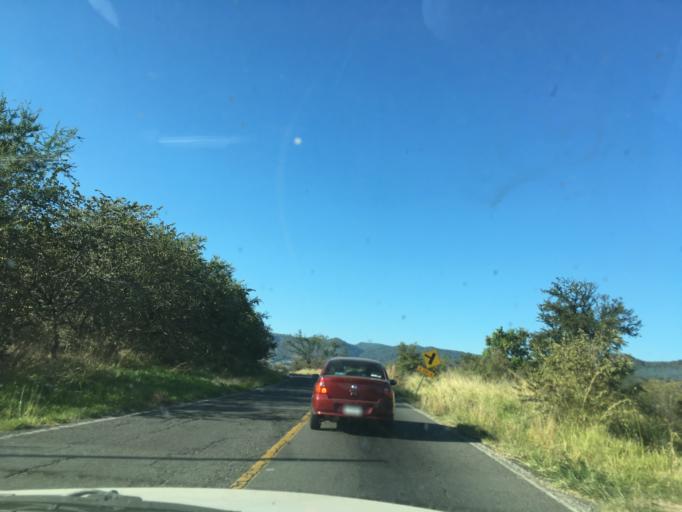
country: MX
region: Michoacan
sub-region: Gabriel Zamora
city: Lombardia
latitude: 19.2360
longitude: -102.0496
